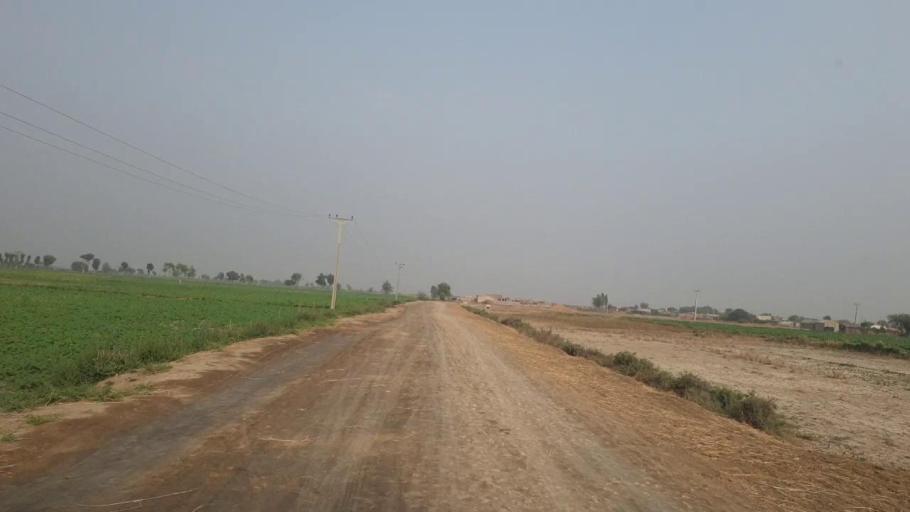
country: PK
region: Sindh
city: Mirpur Batoro
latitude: 24.5589
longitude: 68.4188
